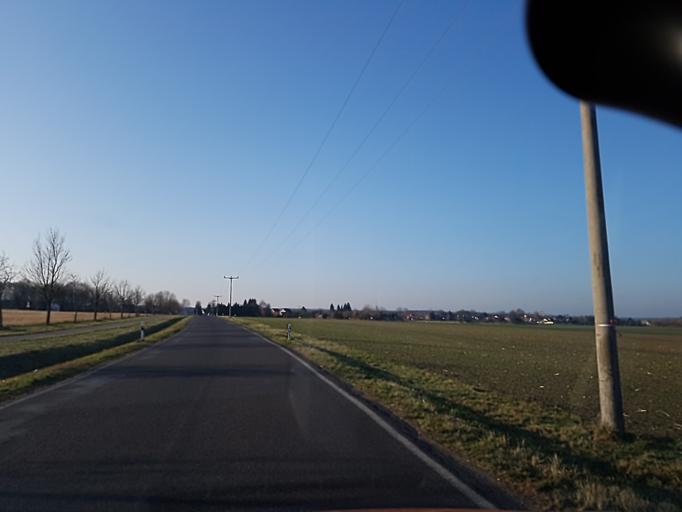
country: DE
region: Brandenburg
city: Ruckersdorf
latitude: 51.5665
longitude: 13.5590
